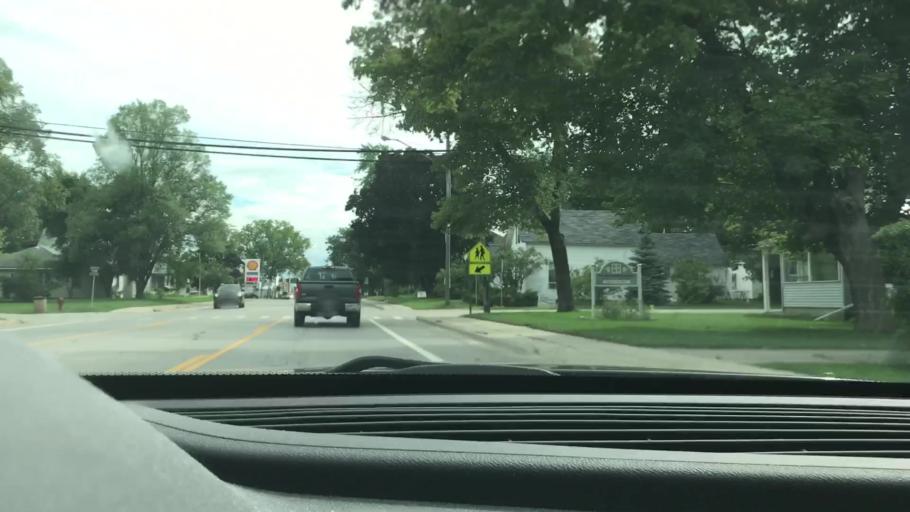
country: US
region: Michigan
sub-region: Missaukee County
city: Lake City
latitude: 44.3372
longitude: -85.2148
